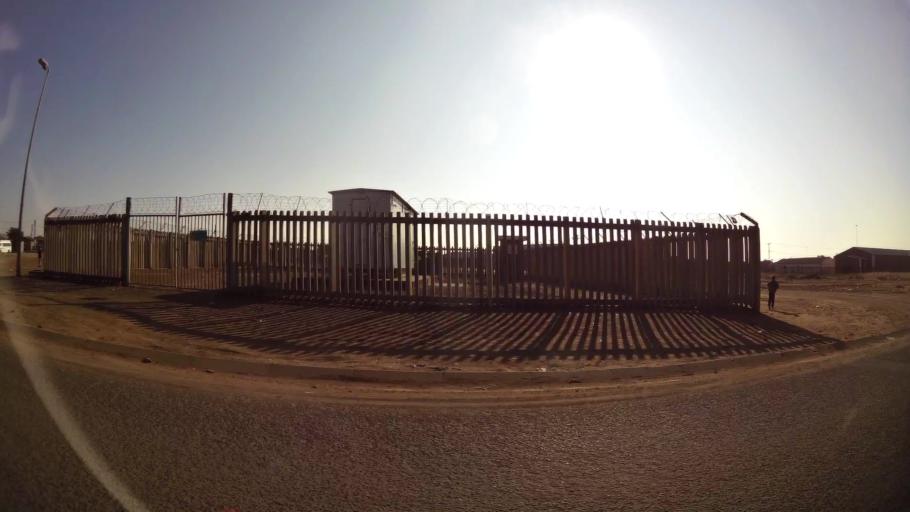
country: ZA
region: Orange Free State
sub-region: Mangaung Metropolitan Municipality
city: Bloemfontein
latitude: -29.1997
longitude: 26.2258
